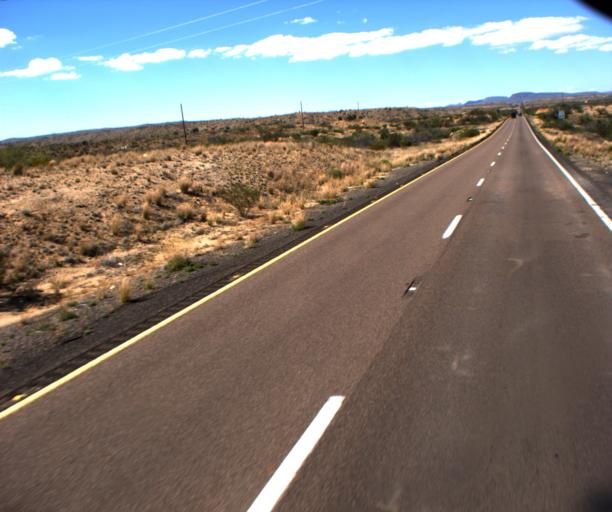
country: US
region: Arizona
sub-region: Mohave County
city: Kingman
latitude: 35.0293
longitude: -113.6642
